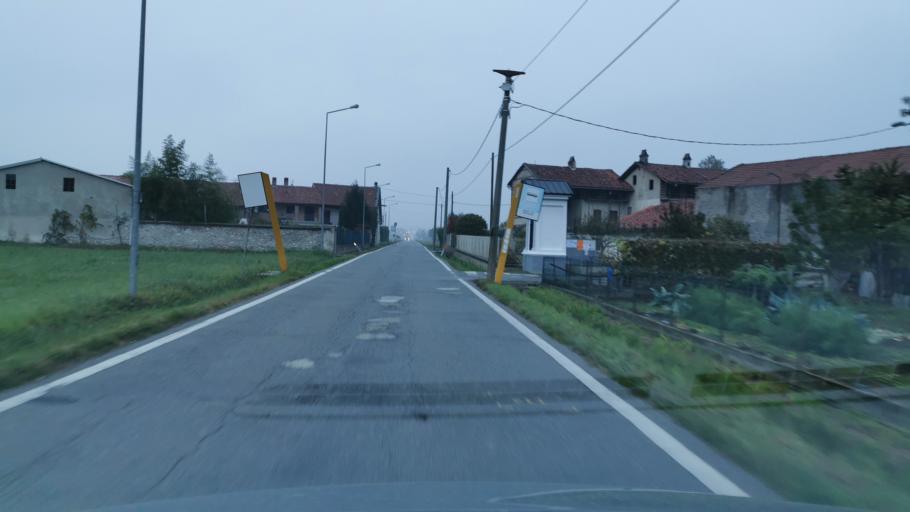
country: IT
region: Piedmont
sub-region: Provincia di Torino
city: Ciconio
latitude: 45.3342
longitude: 7.7630
